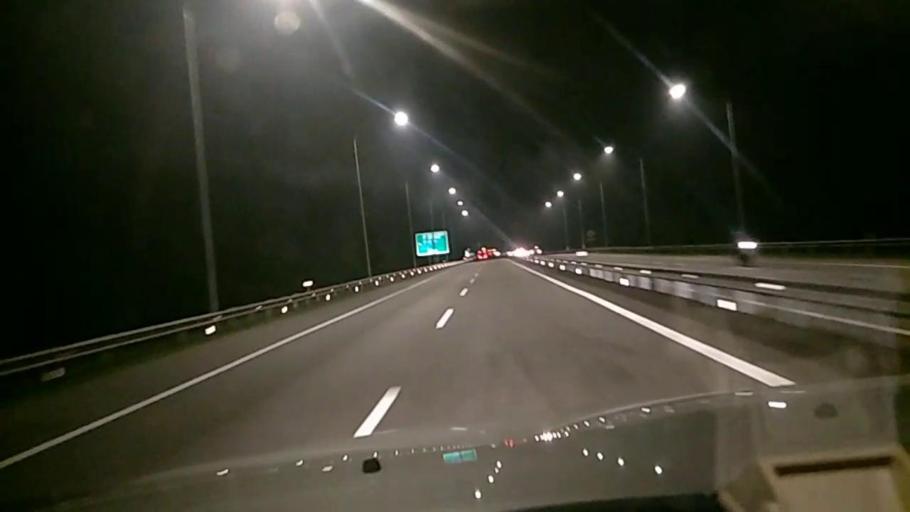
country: MY
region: Perak
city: Bagan Serai
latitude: 5.0721
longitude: 100.5874
